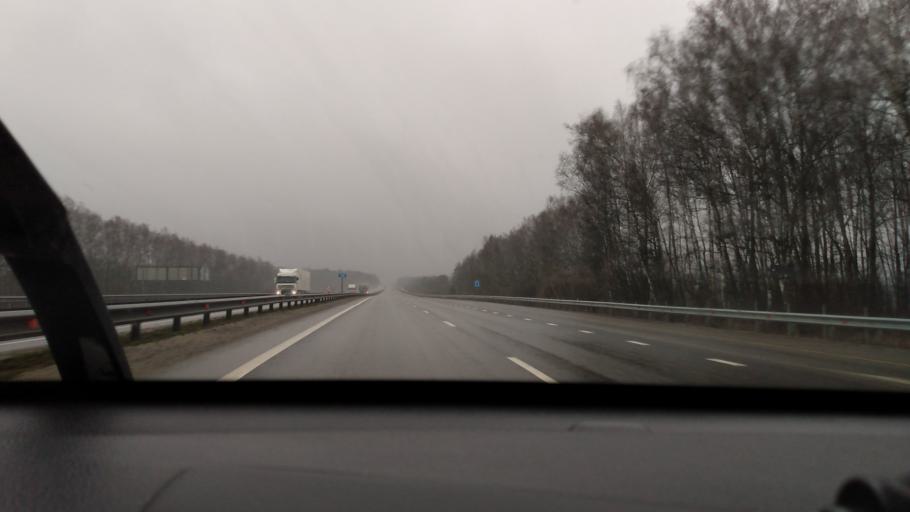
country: RU
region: Tula
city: Venev
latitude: 54.5385
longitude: 38.1654
